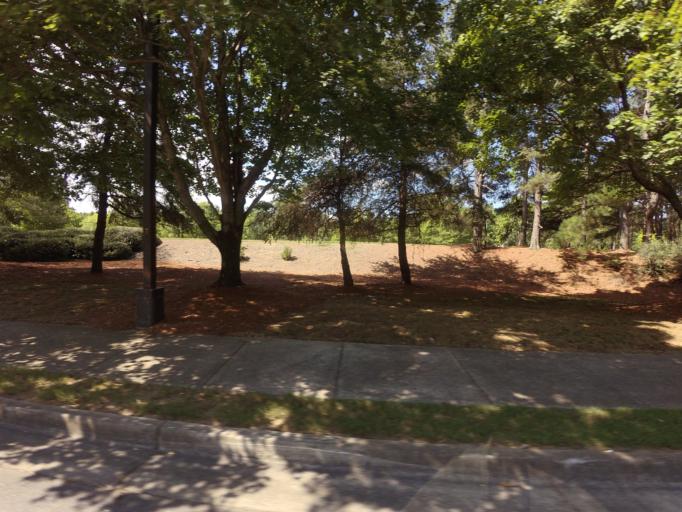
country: US
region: Georgia
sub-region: Fulton County
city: Johns Creek
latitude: 34.0639
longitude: -84.1689
